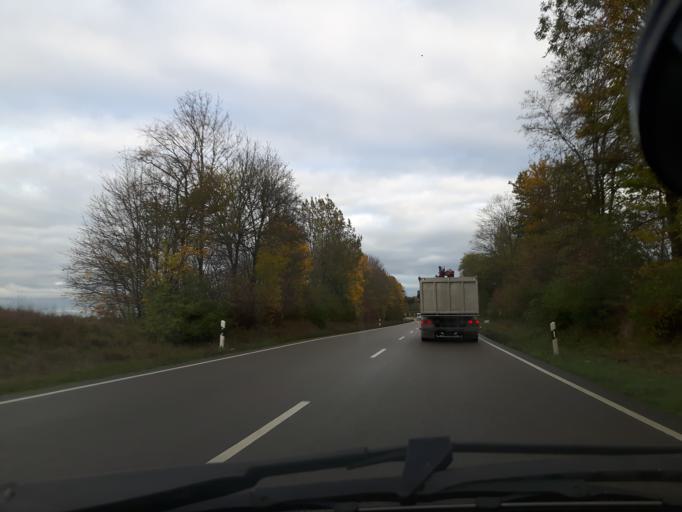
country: DE
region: Bavaria
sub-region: Regierungsbezirk Mittelfranken
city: Weidenbach
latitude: 49.2076
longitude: 10.6644
